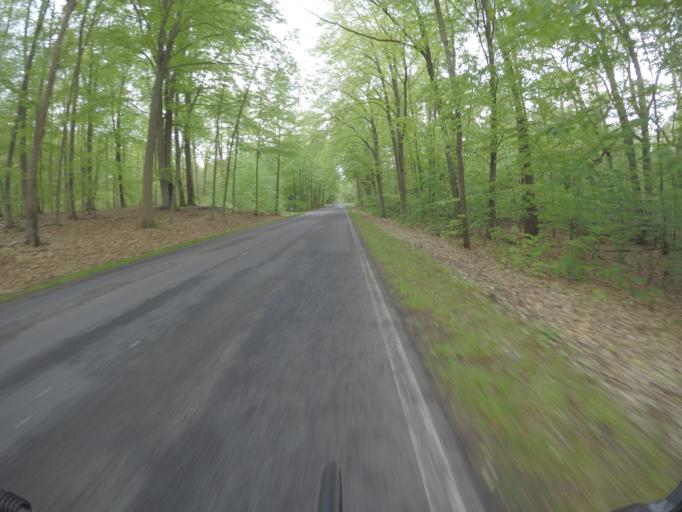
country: DE
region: Brandenburg
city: Joachimsthal
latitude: 52.9187
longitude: 13.7257
